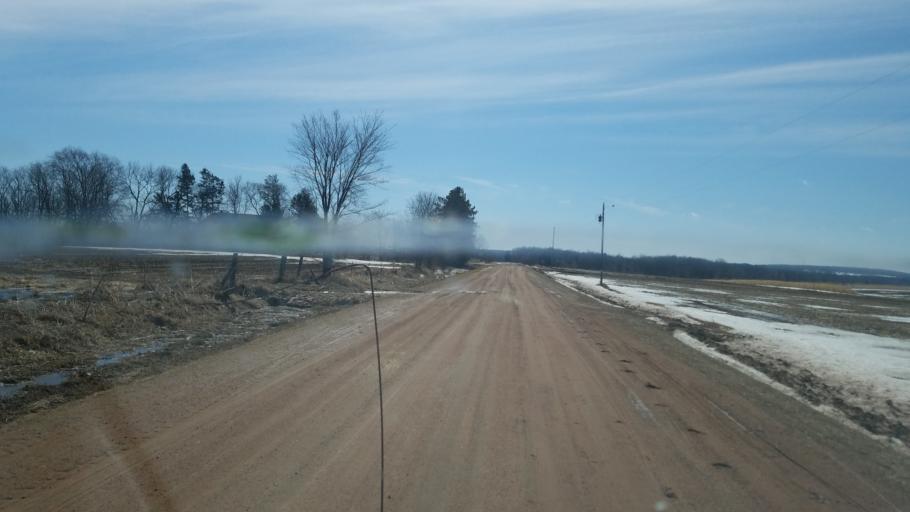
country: US
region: Wisconsin
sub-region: Clark County
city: Loyal
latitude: 44.6124
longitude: -90.4272
